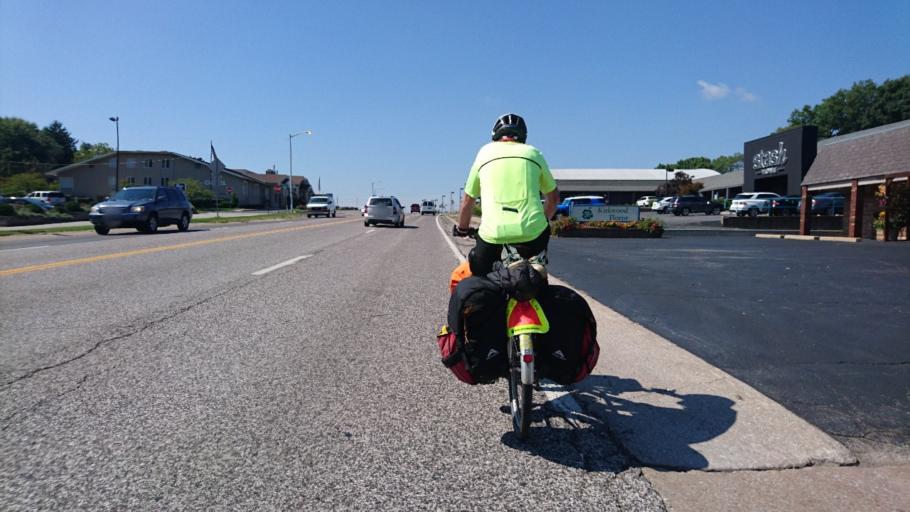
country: US
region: Missouri
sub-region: Saint Louis County
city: Kirkwood
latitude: 38.6006
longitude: -90.4020
